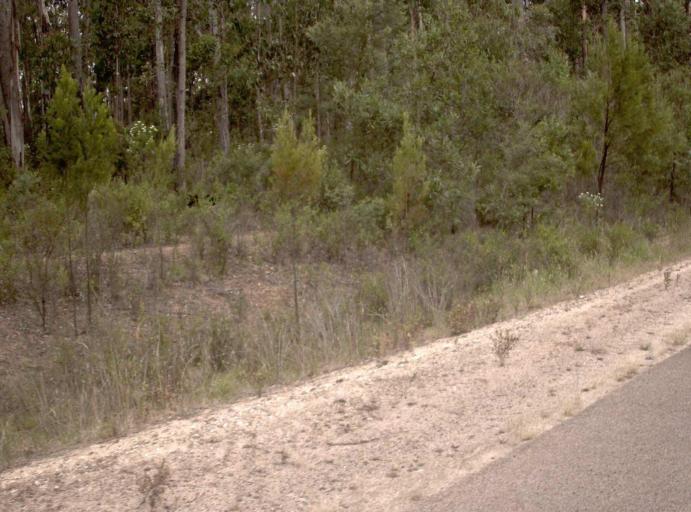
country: AU
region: Victoria
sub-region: East Gippsland
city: Lakes Entrance
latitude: -37.7126
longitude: 148.0737
